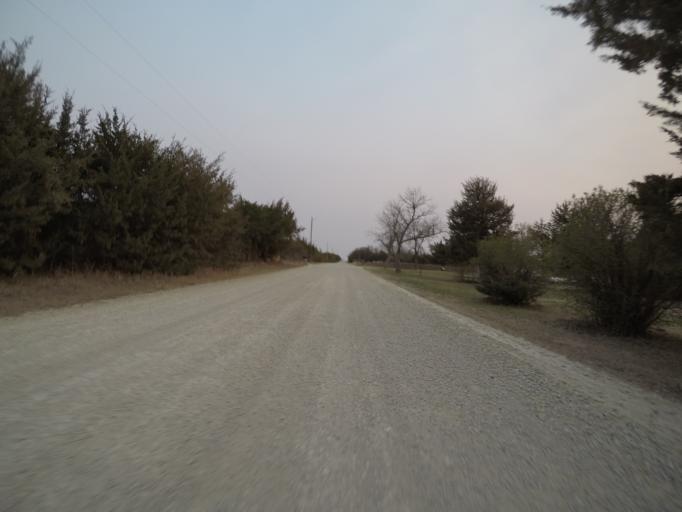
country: US
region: Kansas
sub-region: Riley County
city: Manhattan
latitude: 39.2435
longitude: -96.6538
